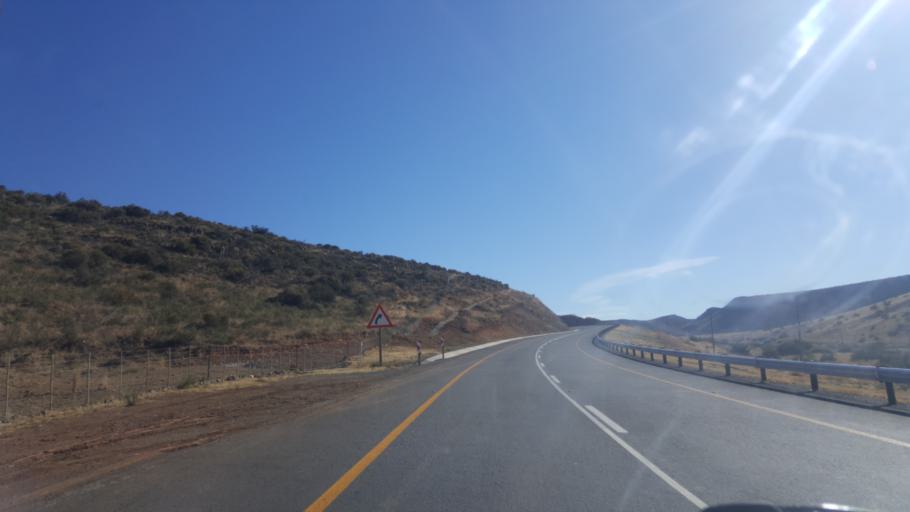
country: ZA
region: Eastern Cape
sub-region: Chris Hani District Municipality
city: Middelburg
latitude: -31.3828
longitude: 25.0325
